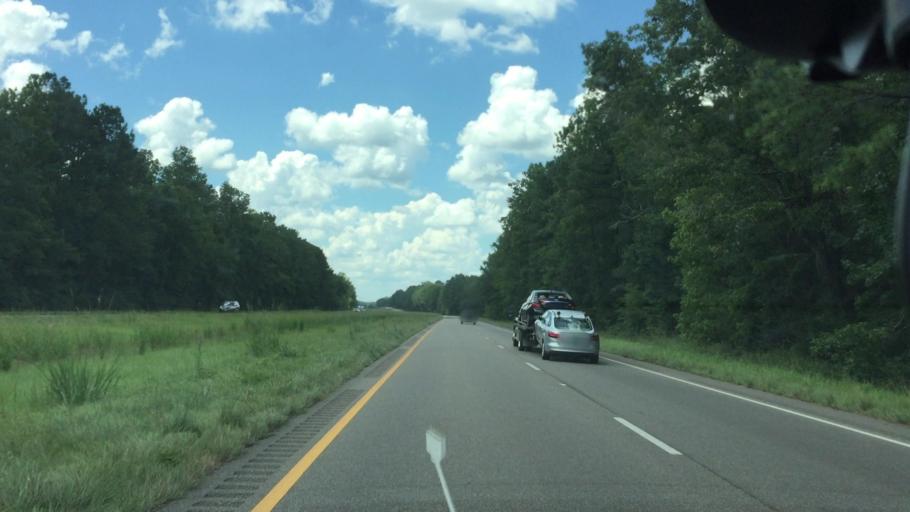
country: US
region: Alabama
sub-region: Montgomery County
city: Pike Road
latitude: 32.1334
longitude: -86.0866
